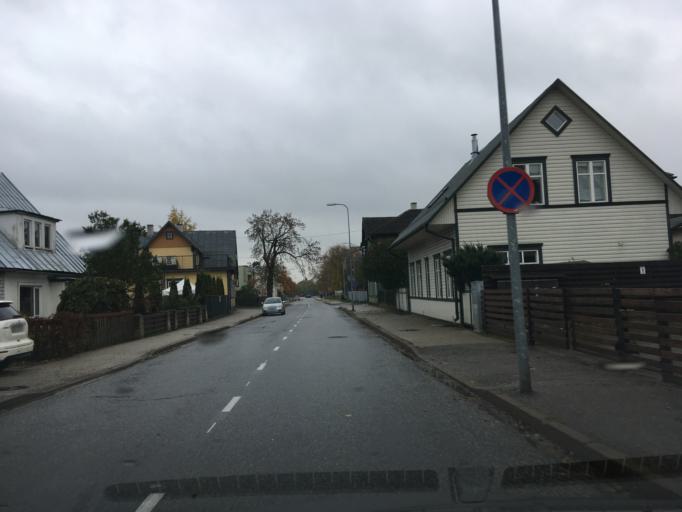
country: EE
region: Paernumaa
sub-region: Paernu linn
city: Parnu
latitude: 58.3758
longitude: 24.5185
